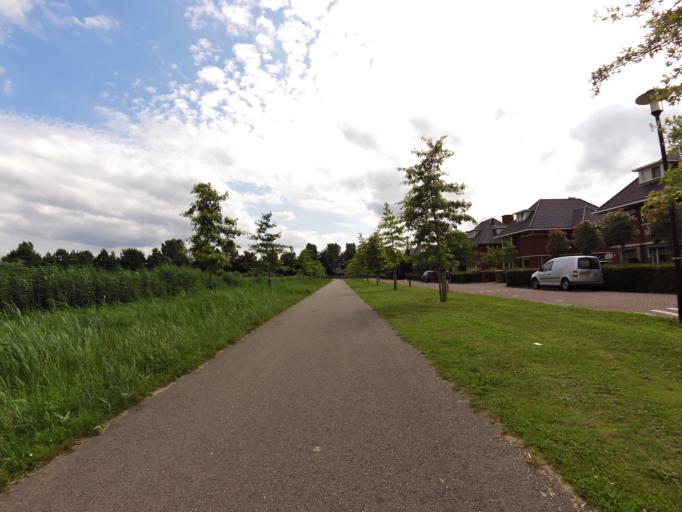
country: NL
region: South Holland
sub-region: Gemeente Sliedrecht
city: Sliedrecht
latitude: 51.7916
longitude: 4.7325
